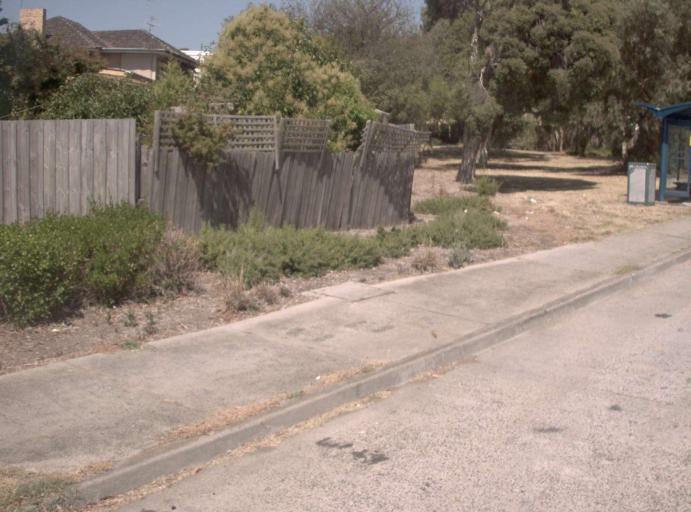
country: AU
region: Victoria
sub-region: Manningham
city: Bulleen
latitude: -37.7695
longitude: 145.0986
